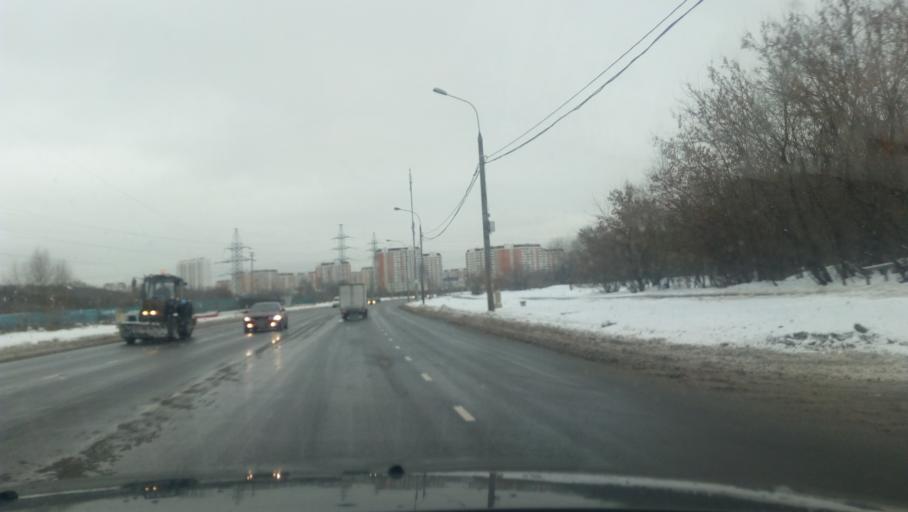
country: RU
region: Moscow
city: Zhulebino
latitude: 55.7206
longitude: 37.8691
